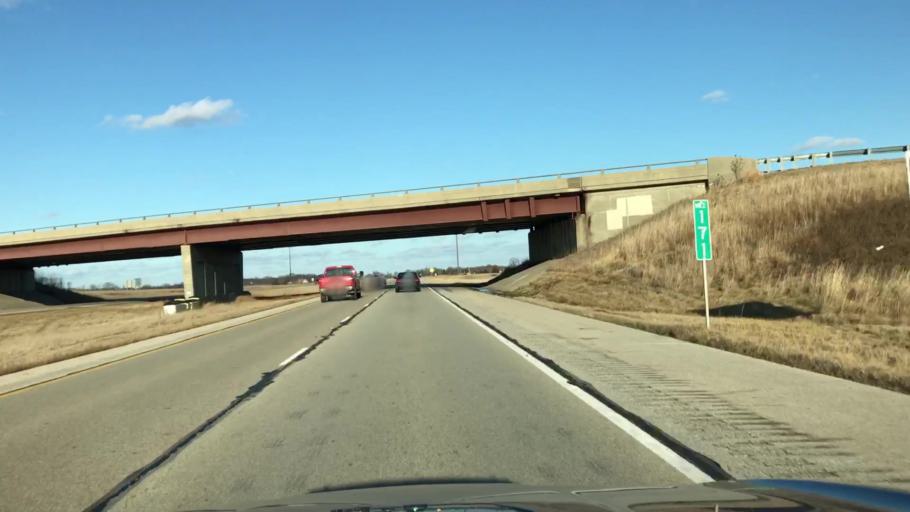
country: US
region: Illinois
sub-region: McLean County
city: Hudson
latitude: 40.5713
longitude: -88.9013
